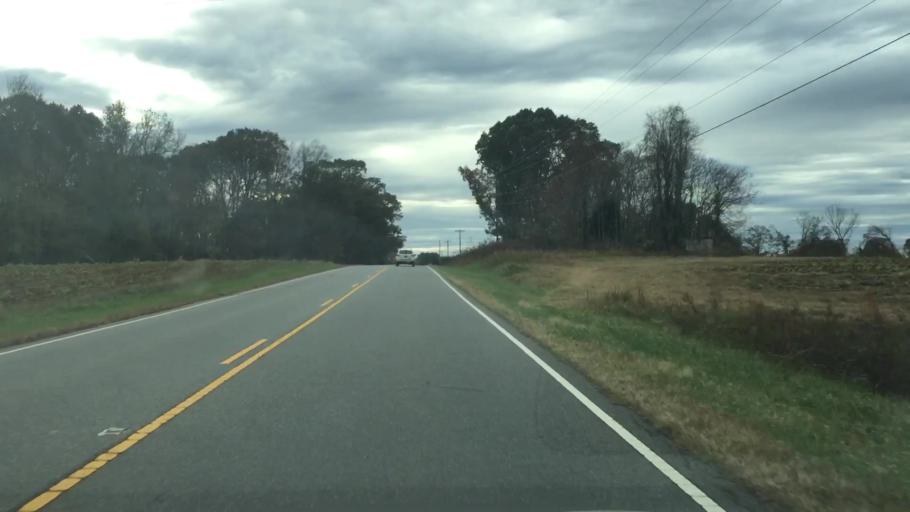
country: US
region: North Carolina
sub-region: Guilford County
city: Summerfield
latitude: 36.2749
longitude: -79.8201
